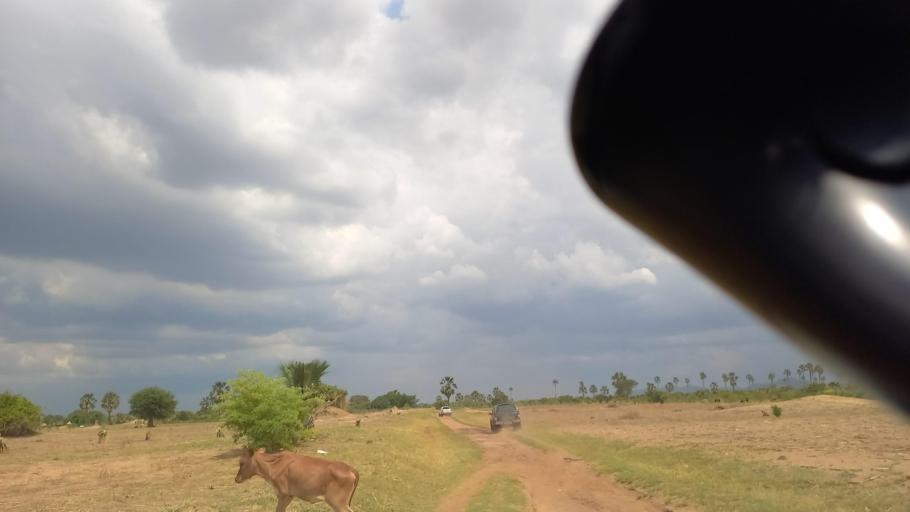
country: ZM
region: Lusaka
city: Kafue
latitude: -15.8311
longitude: 28.0646
